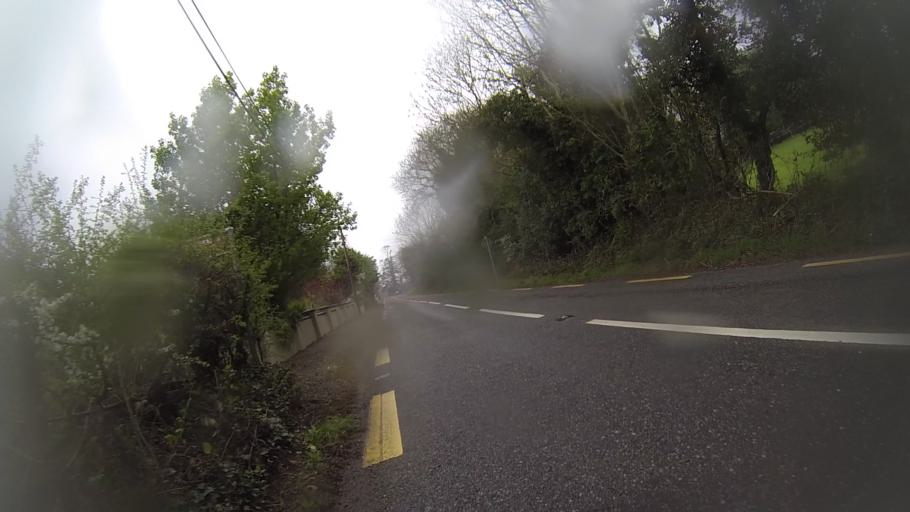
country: IE
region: Munster
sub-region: Ciarrai
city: Kenmare
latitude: 51.8166
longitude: -9.5353
